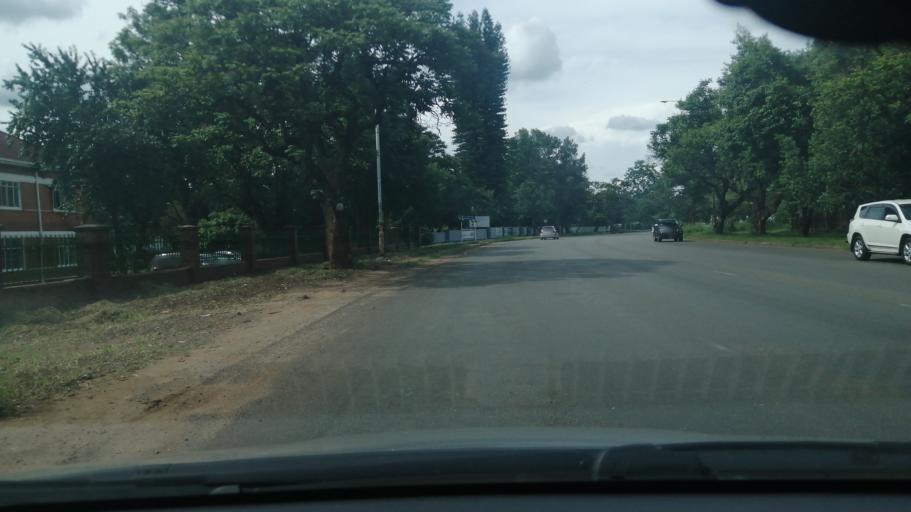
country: ZW
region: Harare
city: Harare
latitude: -17.8027
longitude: 31.0443
